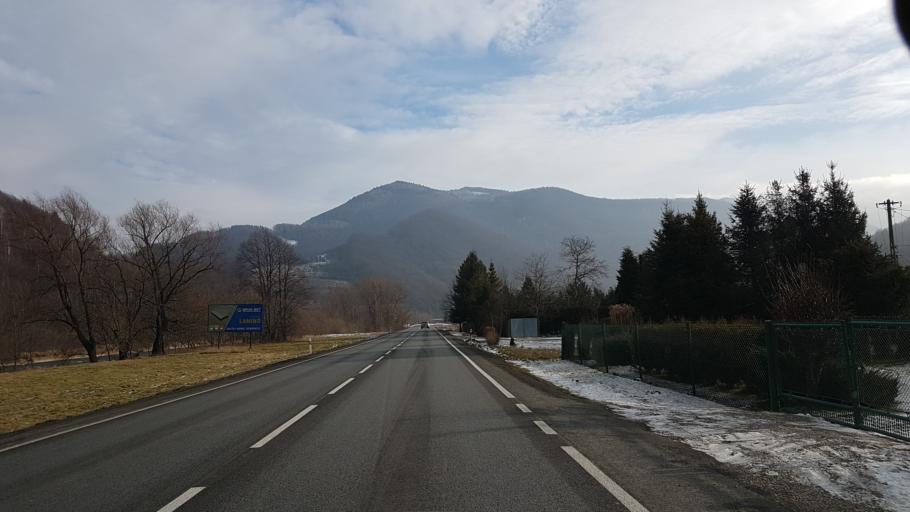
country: PL
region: Lesser Poland Voivodeship
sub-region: Powiat nowosadecki
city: Rytro
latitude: 49.5000
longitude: 20.6685
